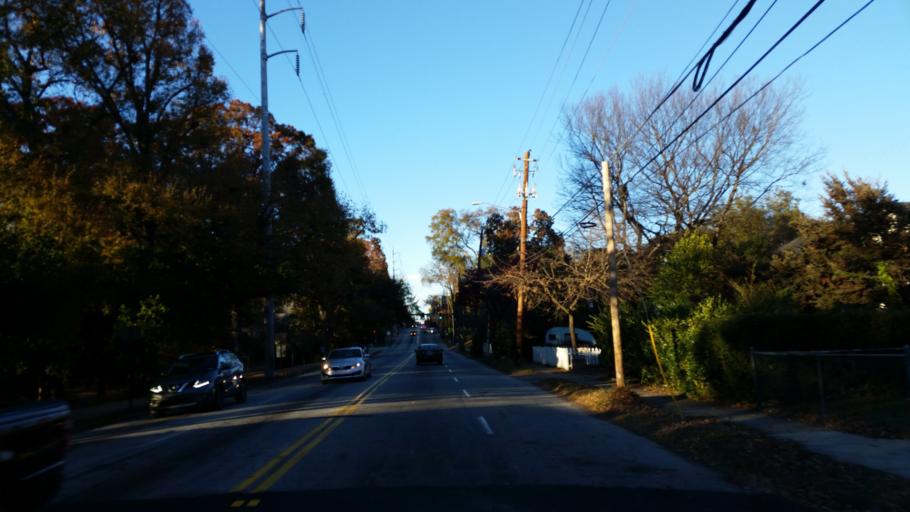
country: US
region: Georgia
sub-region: Fulton County
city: Atlanta
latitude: 33.7358
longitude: -84.3682
